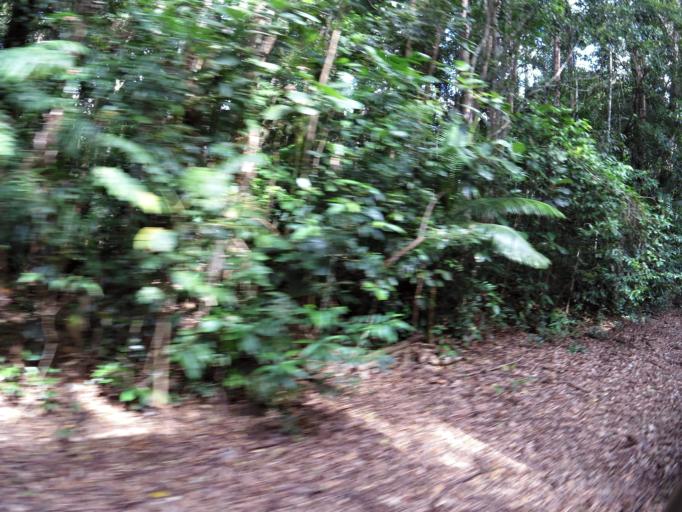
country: AU
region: Queensland
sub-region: Tablelands
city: Kuranda
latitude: -16.8249
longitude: 145.6403
